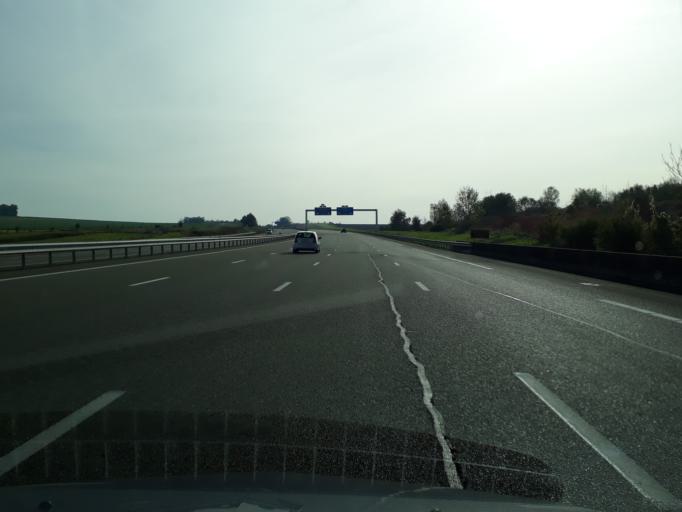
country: FR
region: Bourgogne
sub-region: Departement de l'Yonne
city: Soucy
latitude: 48.2789
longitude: 3.2744
